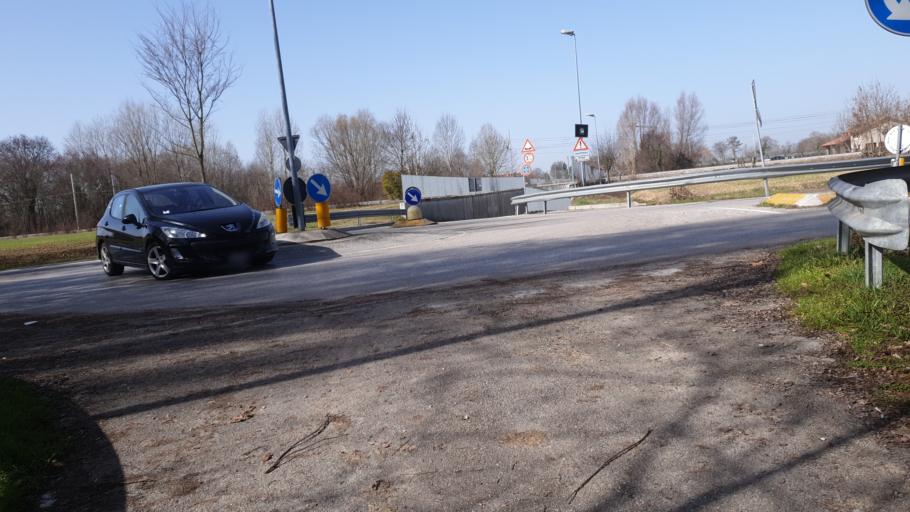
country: IT
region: Veneto
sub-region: Provincia di Padova
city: Camposampiero
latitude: 45.5517
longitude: 11.9226
